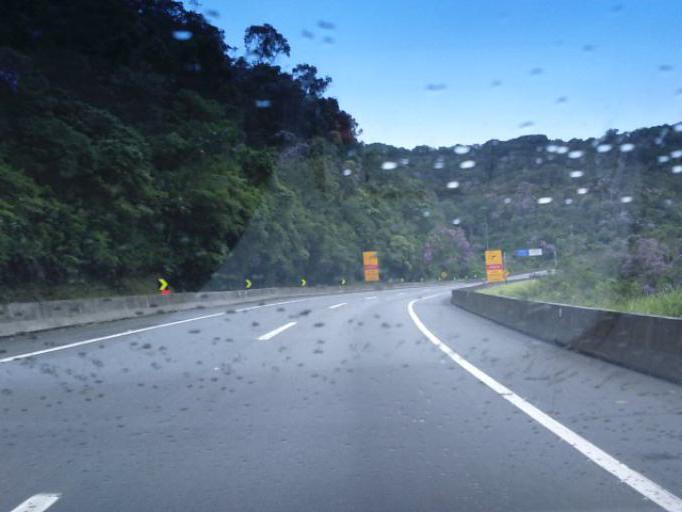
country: BR
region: Sao Paulo
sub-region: Cajati
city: Cajati
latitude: -24.9639
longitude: -48.4310
